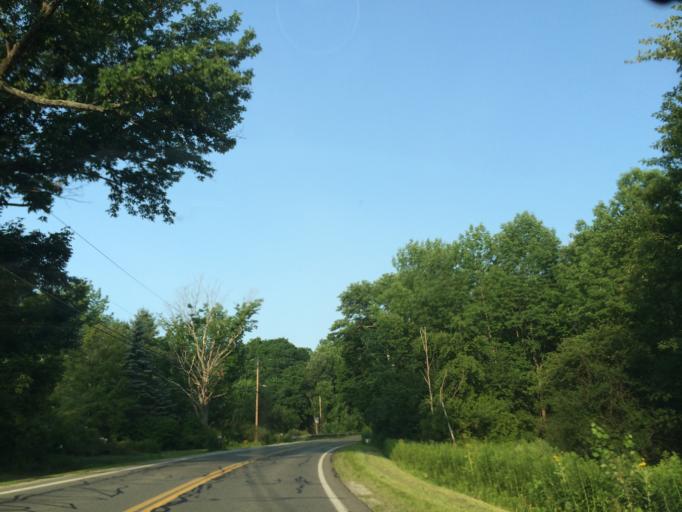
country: US
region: Massachusetts
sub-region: Berkshire County
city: Richmond
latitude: 42.3948
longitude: -73.3849
